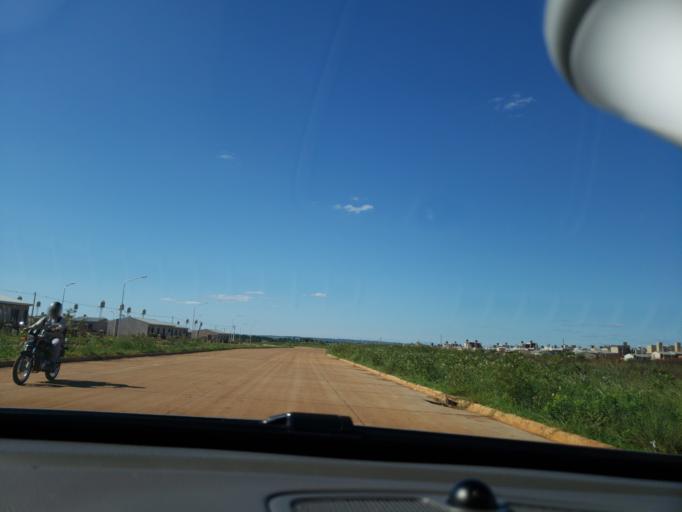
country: AR
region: Misiones
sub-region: Departamento de Capital
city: Posadas
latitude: -27.4058
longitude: -55.9886
